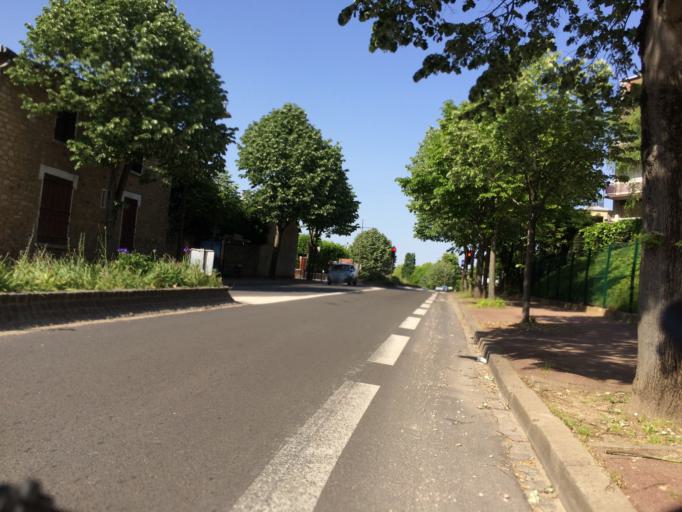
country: FR
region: Ile-de-France
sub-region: Departement des Hauts-de-Seine
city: Chatenay-Malabry
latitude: 48.7674
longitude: 2.2727
